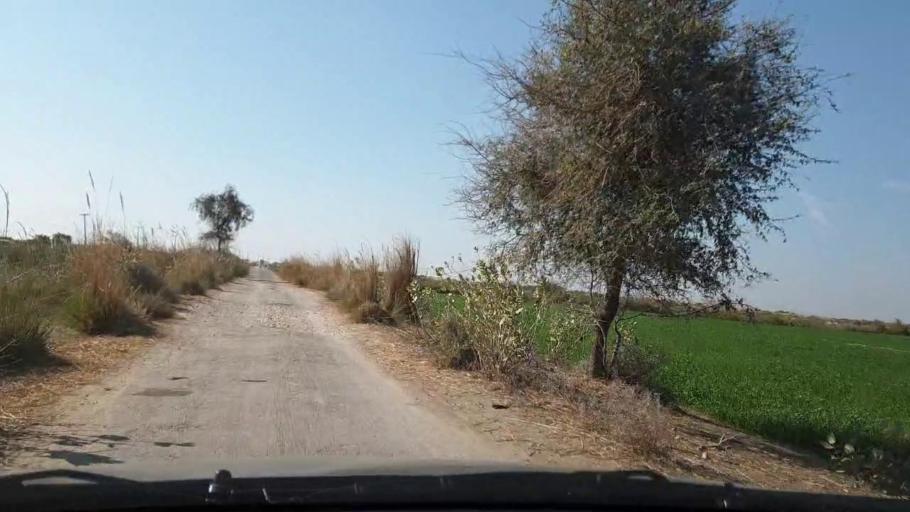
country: PK
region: Sindh
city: Khadro
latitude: 26.2678
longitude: 68.8025
